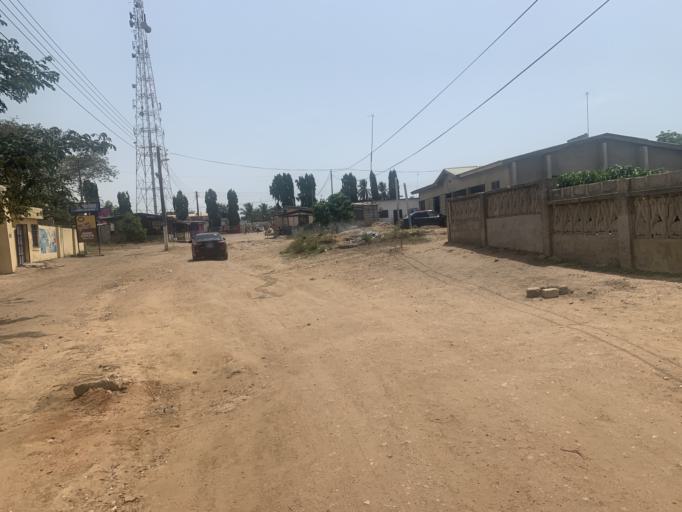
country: GH
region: Central
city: Winneba
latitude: 5.3490
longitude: -0.6305
